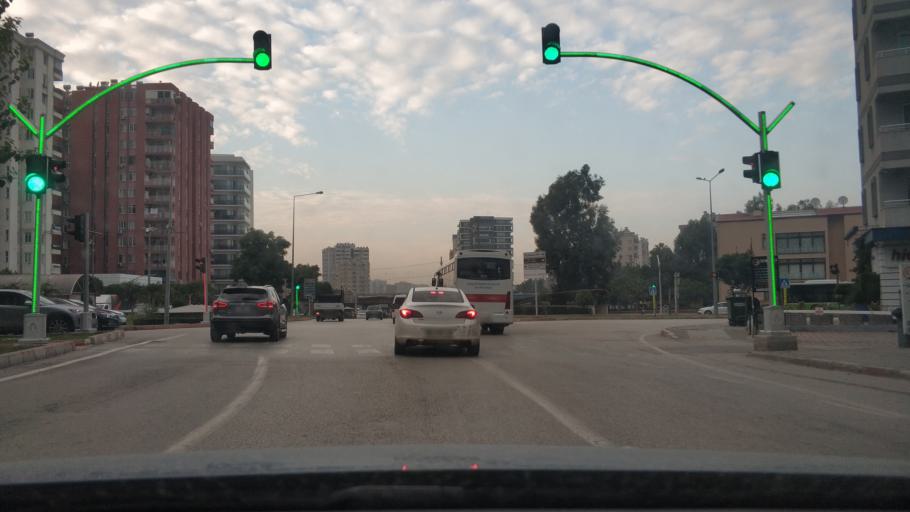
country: TR
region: Adana
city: Adana
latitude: 37.0015
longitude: 35.3142
